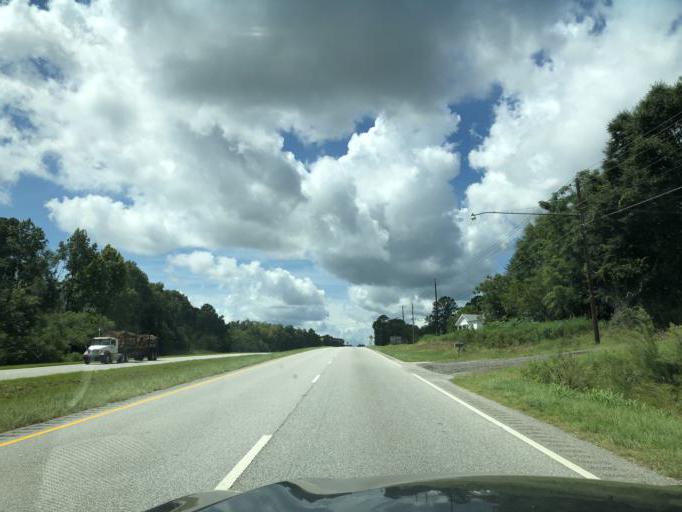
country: US
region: Alabama
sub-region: Barbour County
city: Eufaula
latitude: 31.9334
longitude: -85.1380
